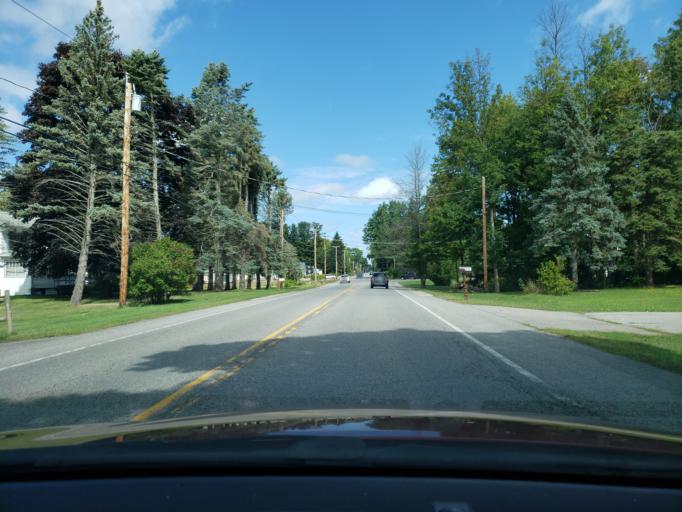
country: US
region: New York
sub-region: Monroe County
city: Greece
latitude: 43.2379
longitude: -77.7334
